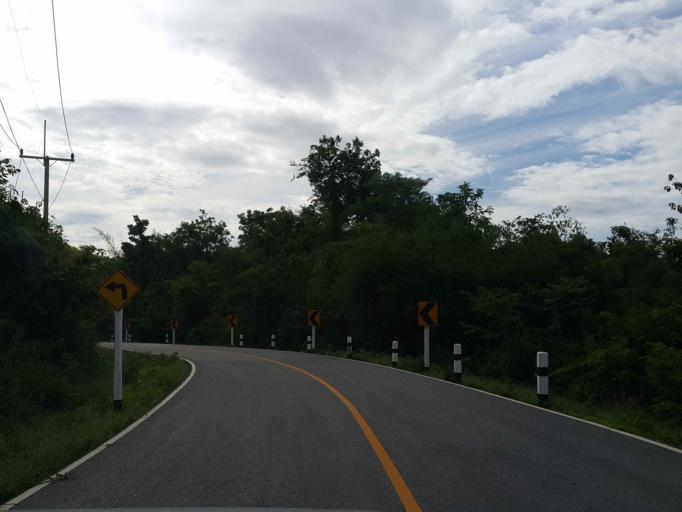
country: TH
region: Sukhothai
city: Thung Saliam
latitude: 17.2457
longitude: 99.4899
